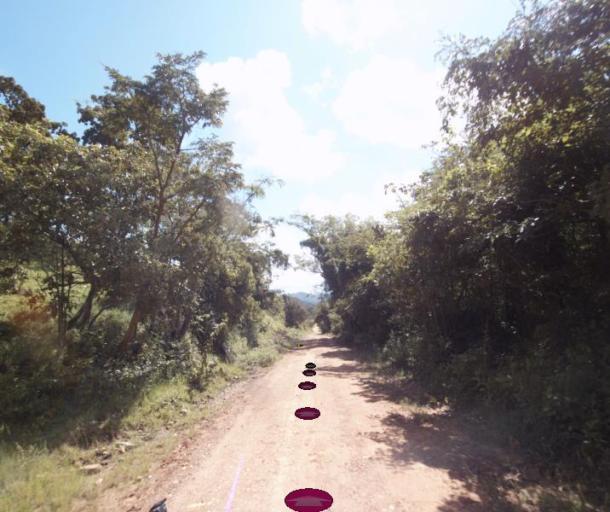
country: BR
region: Goias
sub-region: Pirenopolis
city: Pirenopolis
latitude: -15.7832
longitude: -48.9482
